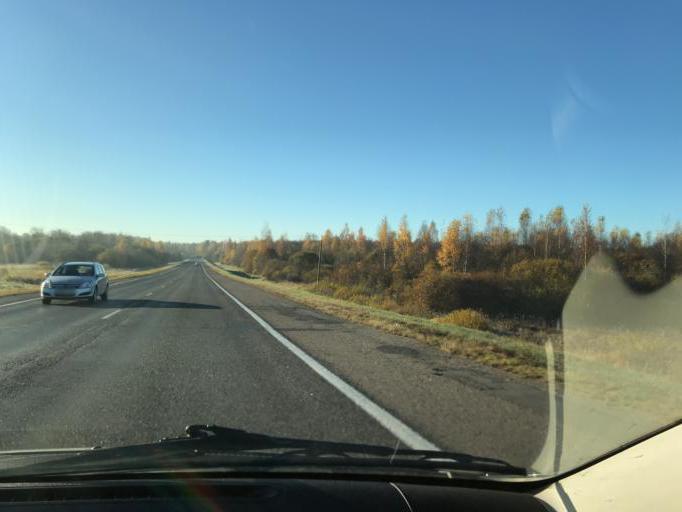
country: BY
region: Vitebsk
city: Vitebsk
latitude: 54.9066
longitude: 30.3762
